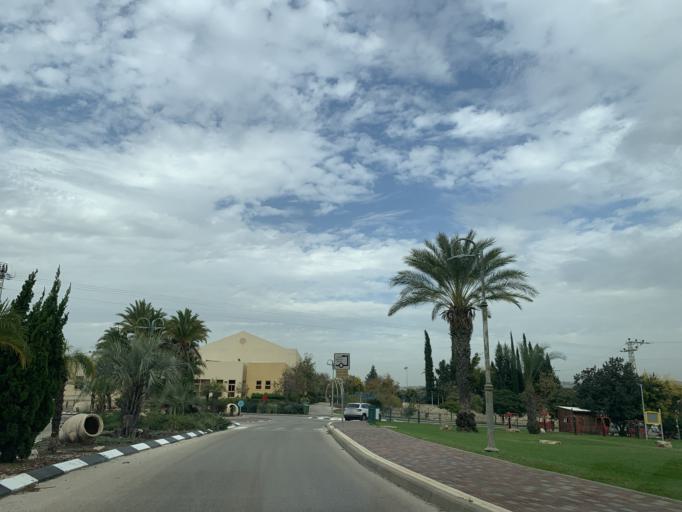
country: IL
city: Nirit
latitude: 32.1451
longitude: 34.9866
